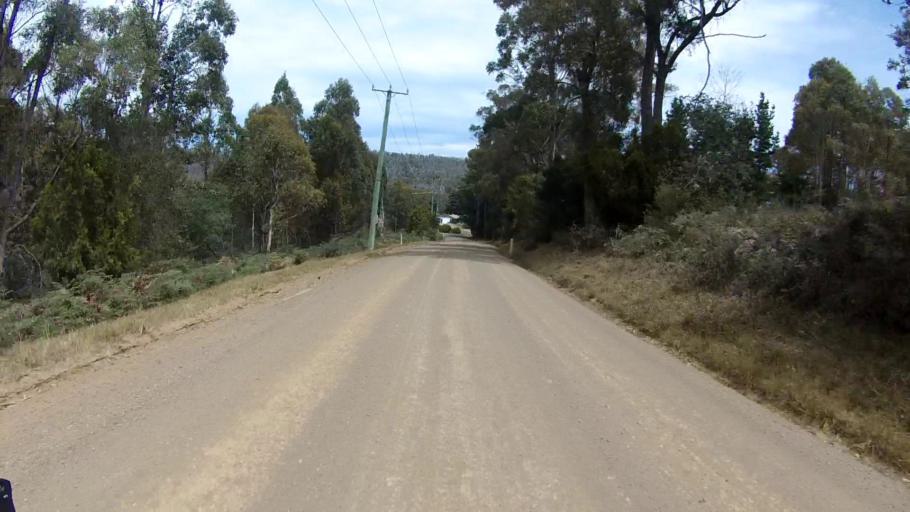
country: AU
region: Tasmania
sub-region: Sorell
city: Sorell
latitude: -42.8026
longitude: 147.6743
